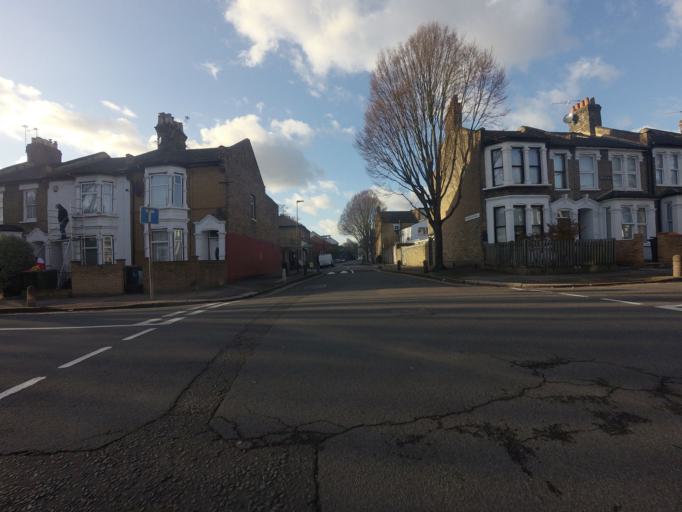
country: GB
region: England
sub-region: Greater London
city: East Ham
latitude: 51.5355
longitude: 0.0143
